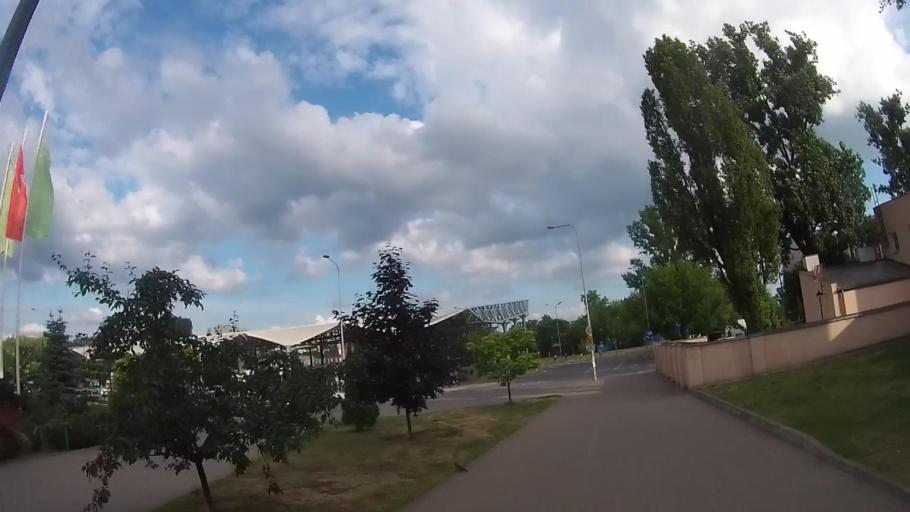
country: PL
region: Masovian Voivodeship
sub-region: Warszawa
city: Praga Polnoc
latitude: 52.2504
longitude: 21.0517
